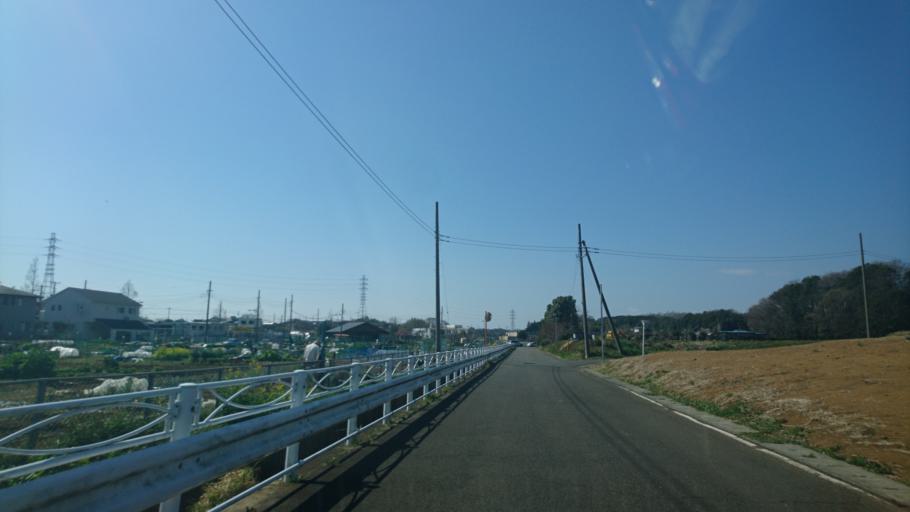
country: JP
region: Kanagawa
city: Fujisawa
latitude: 35.3916
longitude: 139.4359
